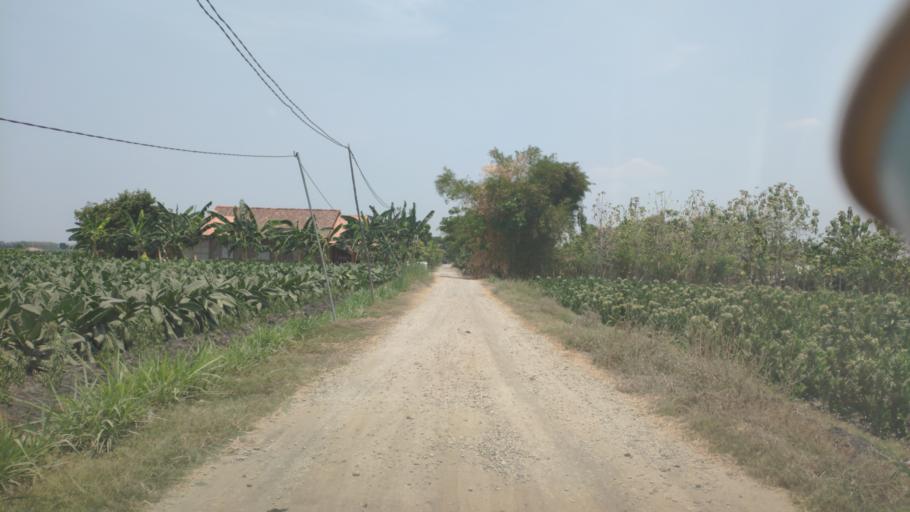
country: ID
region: Central Java
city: Temulus
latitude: -7.2269
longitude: 111.4318
